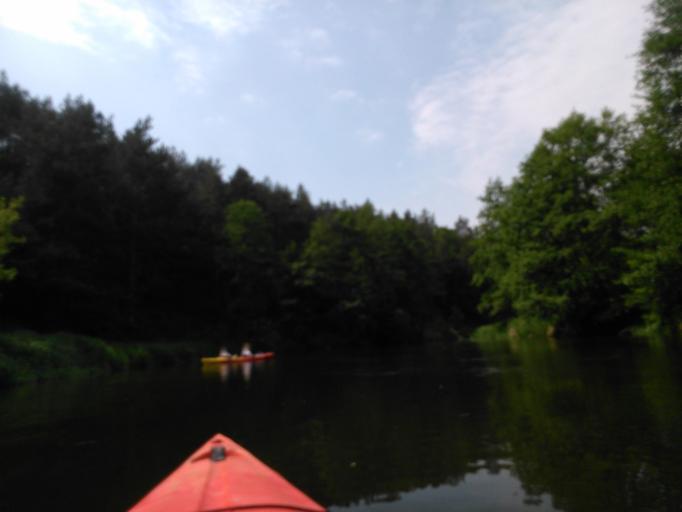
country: PL
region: Kujawsko-Pomorskie
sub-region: Powiat golubsko-dobrzynski
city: Golub-Dobrzyn
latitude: 53.1040
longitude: 19.0400
